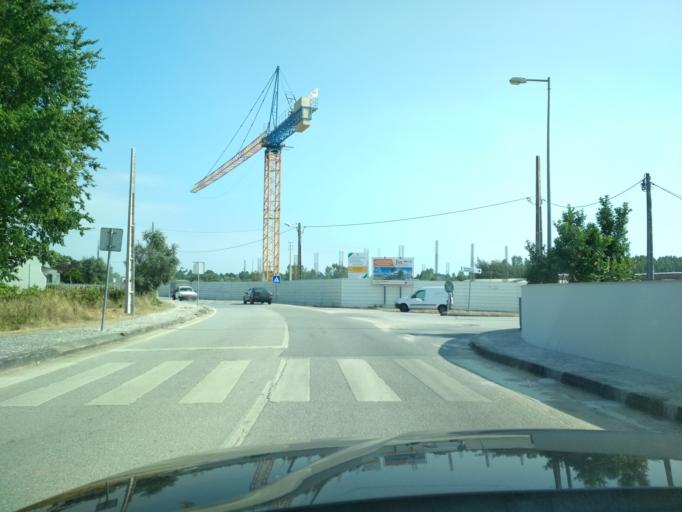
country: PT
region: Aveiro
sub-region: Mealhada
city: Mealhada
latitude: 40.3767
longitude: -8.4578
